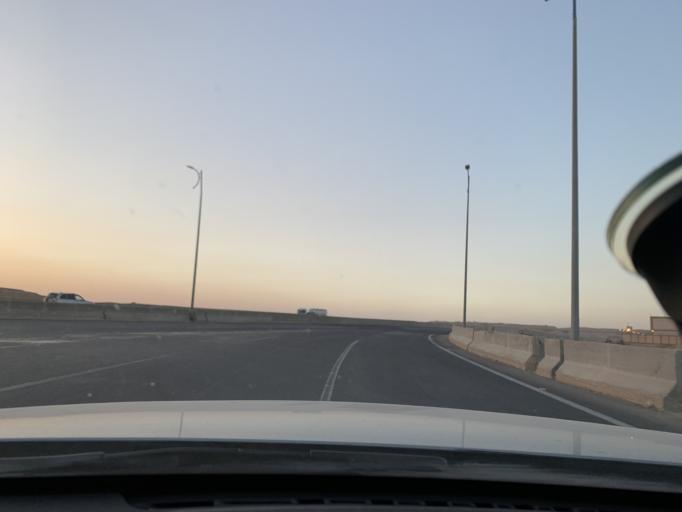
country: EG
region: Muhafazat al Qahirah
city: Halwan
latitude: 29.9357
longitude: 31.5288
